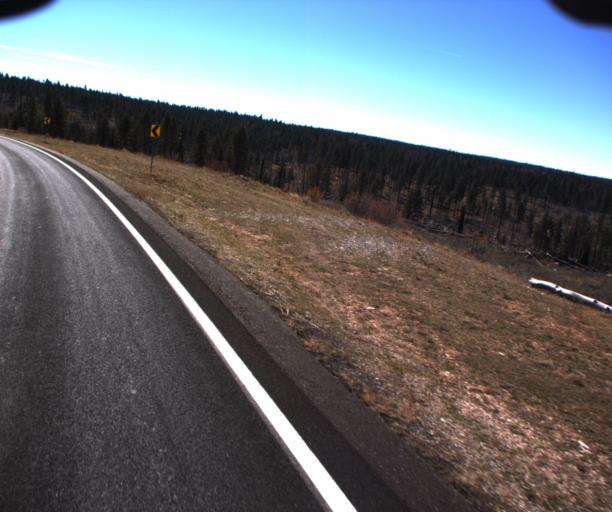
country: US
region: Arizona
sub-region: Coconino County
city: Grand Canyon
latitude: 36.5471
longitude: -112.1806
